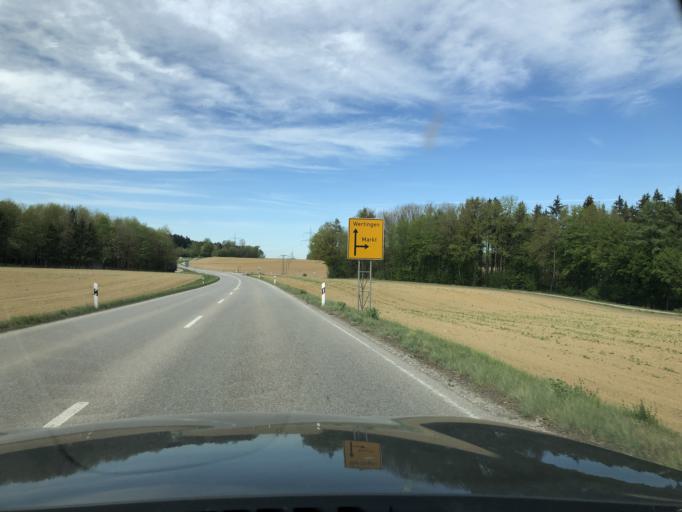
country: DE
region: Bavaria
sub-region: Swabia
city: Biberbach
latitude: 48.5243
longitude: 10.7890
